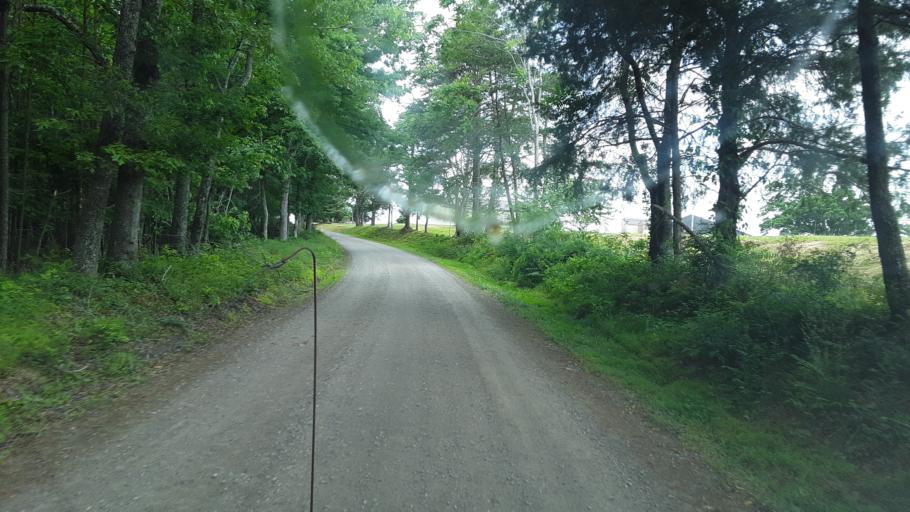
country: US
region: Virginia
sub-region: Pittsylvania County
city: Chatham
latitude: 36.8540
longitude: -79.4391
